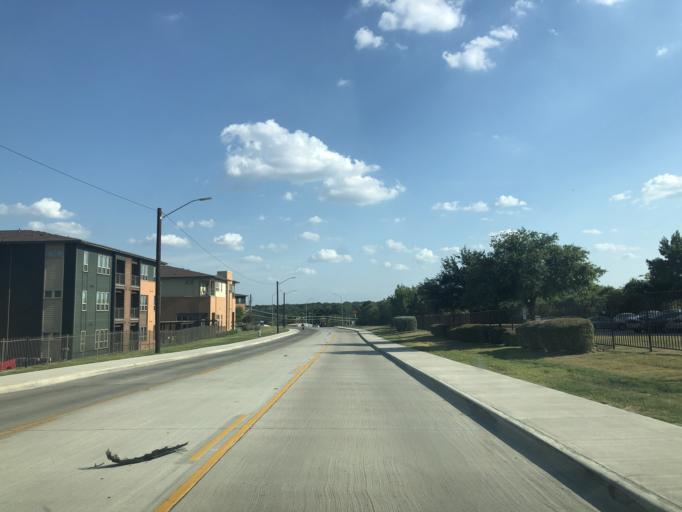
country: US
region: Texas
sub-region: Tarrant County
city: Sansom Park
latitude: 32.8197
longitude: -97.3795
